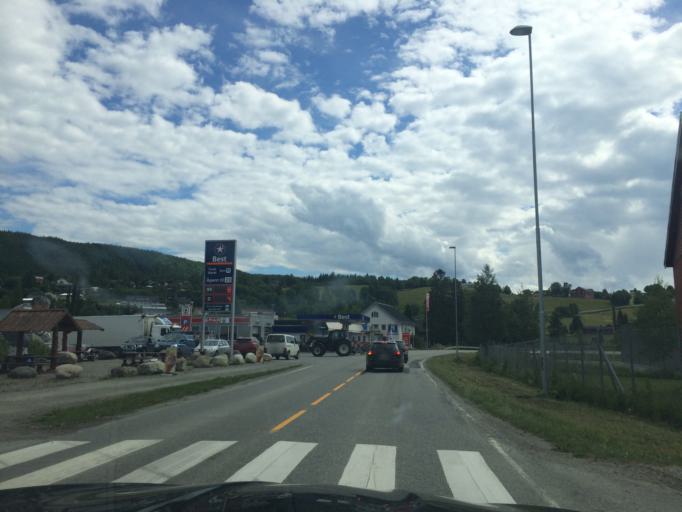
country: NO
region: Sor-Trondelag
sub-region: Selbu
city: Mebonden
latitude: 63.2515
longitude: 11.0934
